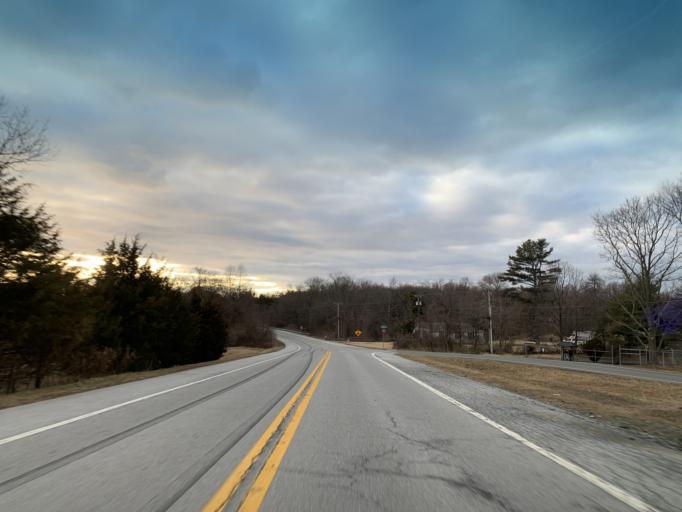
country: US
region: Delaware
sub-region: New Castle County
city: Bear
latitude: 39.5981
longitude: -75.6590
